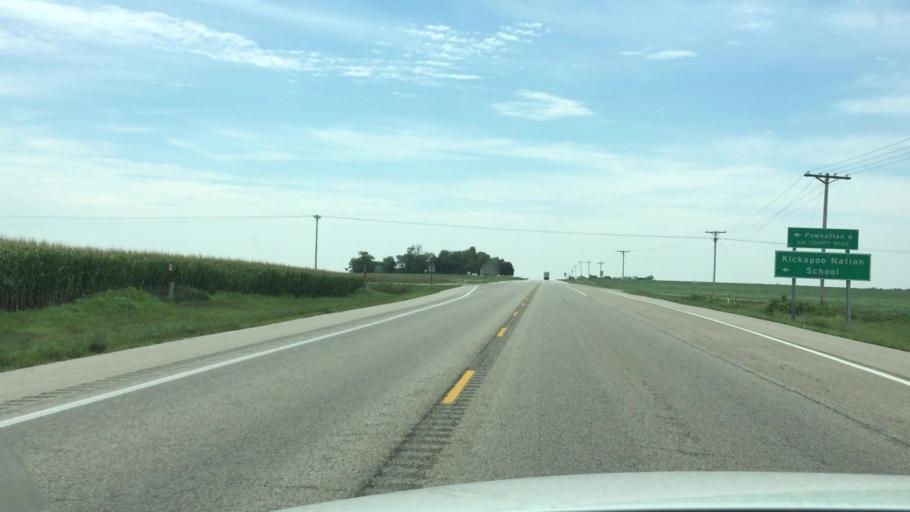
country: US
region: Kansas
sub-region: Nemaha County
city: Sabetha
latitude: 39.7553
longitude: -95.7297
